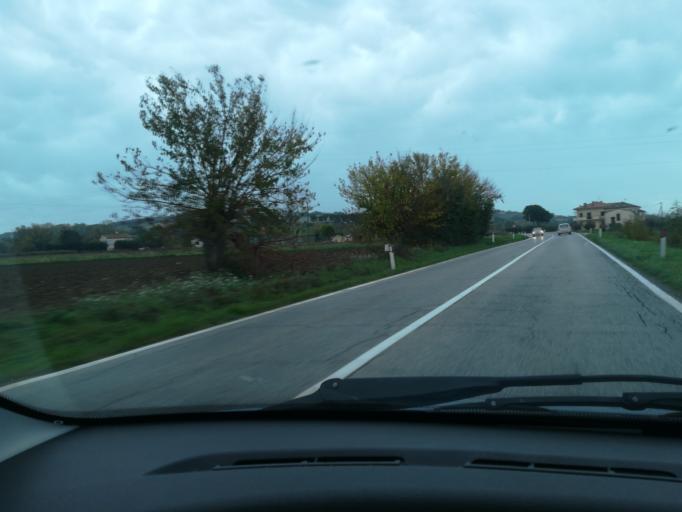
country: IT
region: The Marches
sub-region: Provincia di Macerata
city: Borgo Stazione
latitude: 43.2920
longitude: 13.6614
